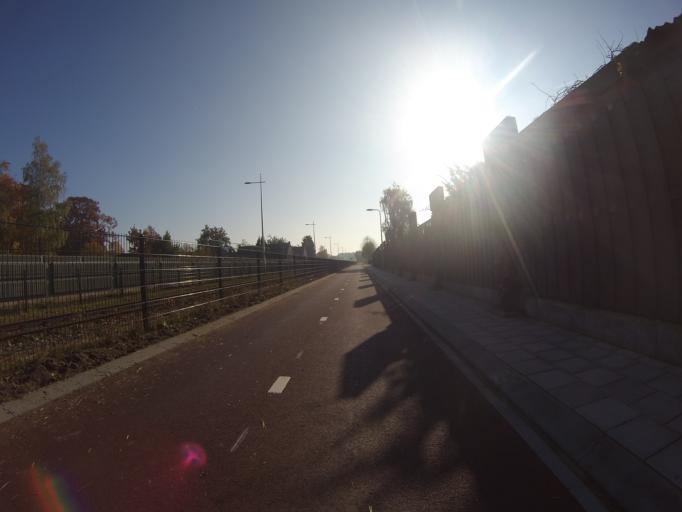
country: NL
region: Utrecht
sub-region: Gemeente Amersfoort
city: Amersfoort
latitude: 52.1478
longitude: 5.3858
